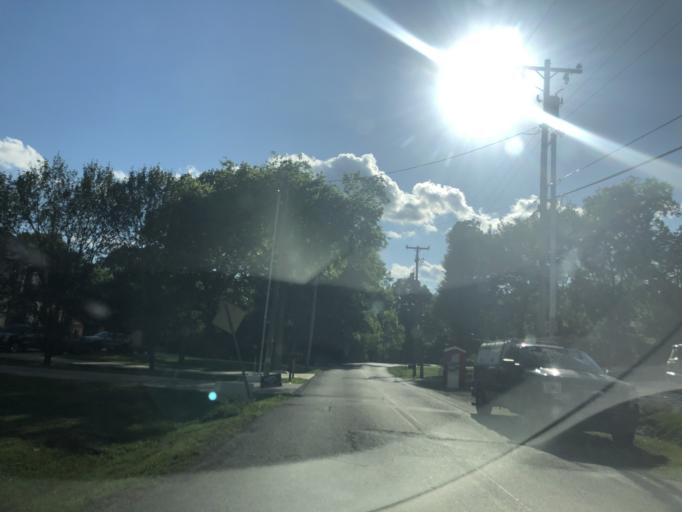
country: US
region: Tennessee
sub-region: Davidson County
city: Oak Hill
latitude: 36.0972
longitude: -86.8175
